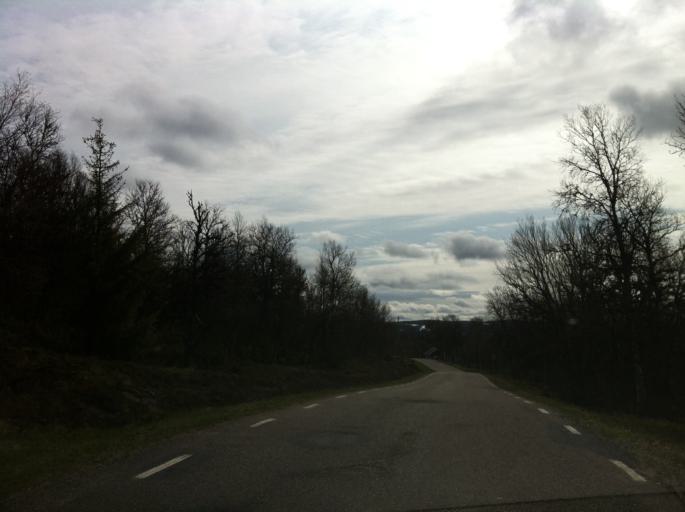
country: NO
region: Hedmark
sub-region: Engerdal
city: Engerdal
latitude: 62.2967
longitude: 12.8065
